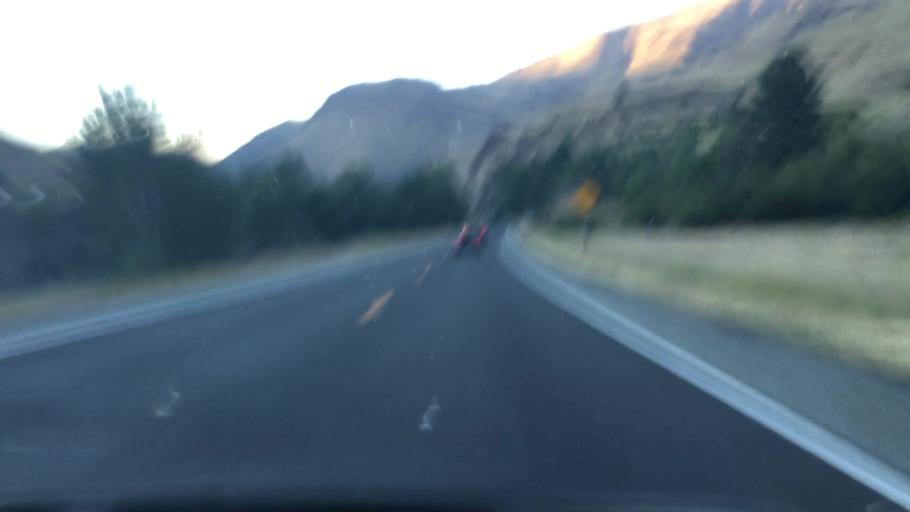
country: US
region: Idaho
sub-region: Valley County
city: McCall
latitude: 45.3249
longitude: -116.3481
